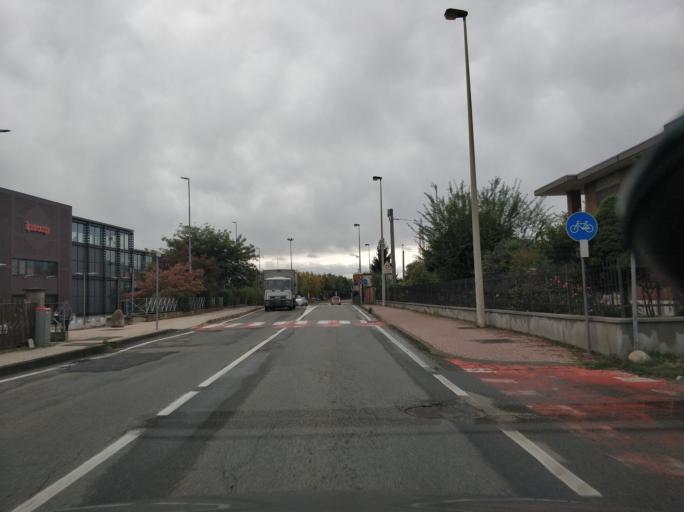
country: IT
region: Piedmont
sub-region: Provincia di Torino
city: Cirie
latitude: 45.2228
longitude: 7.5997
